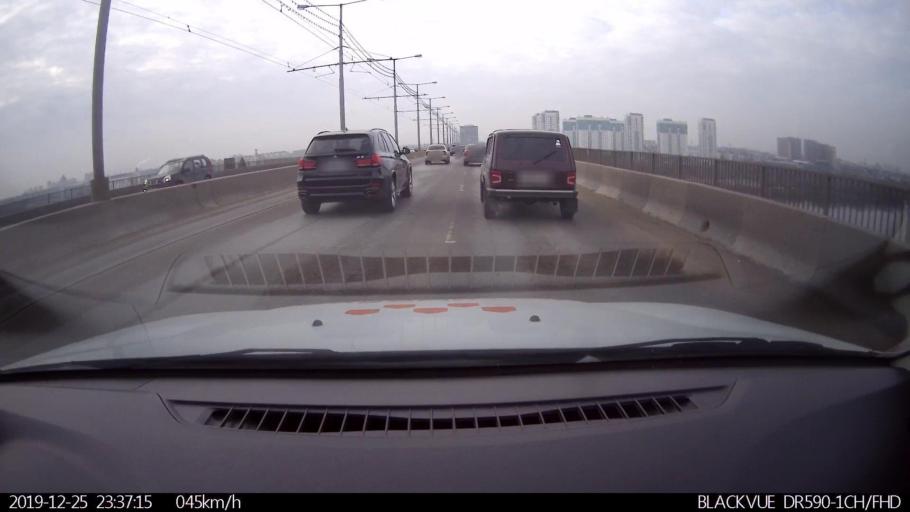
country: RU
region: Nizjnij Novgorod
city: Nizhniy Novgorod
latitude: 56.2984
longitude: 43.9654
